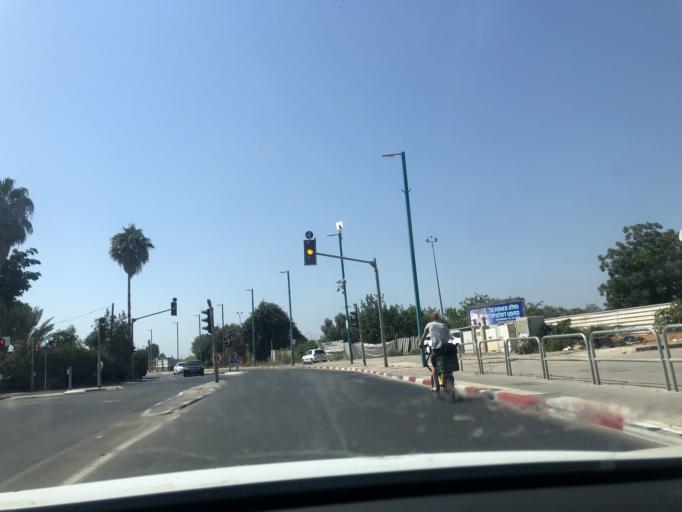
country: IL
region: Central District
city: Lod
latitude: 31.9589
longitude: 34.8922
